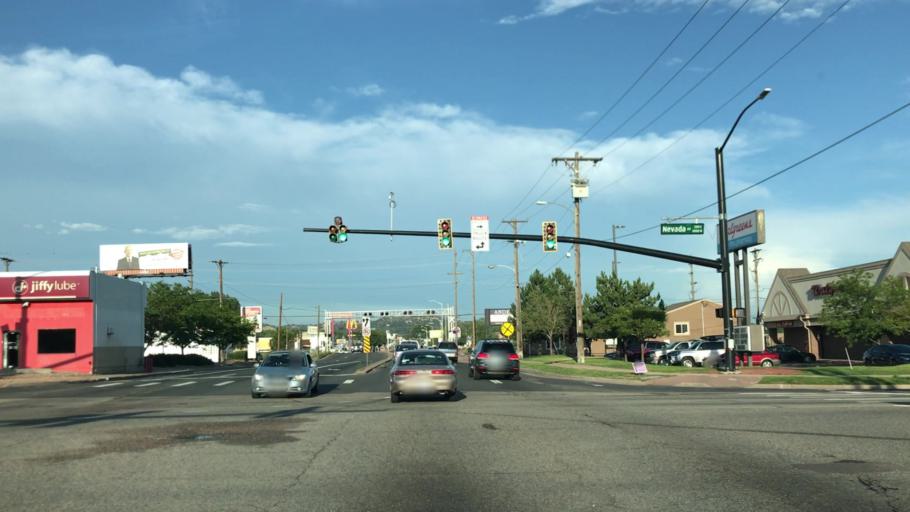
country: US
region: Colorado
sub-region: El Paso County
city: Colorado Springs
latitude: 38.8744
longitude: -104.8197
